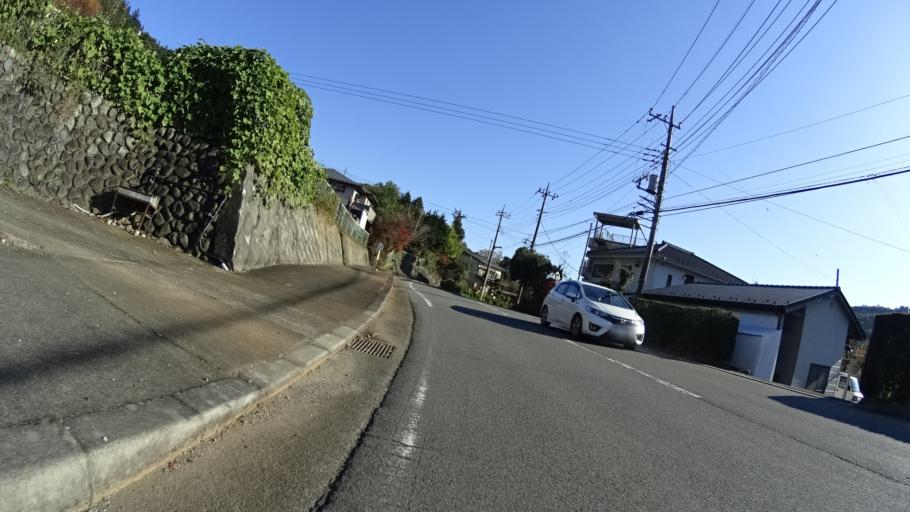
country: JP
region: Yamanashi
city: Uenohara
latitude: 35.6528
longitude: 139.1203
